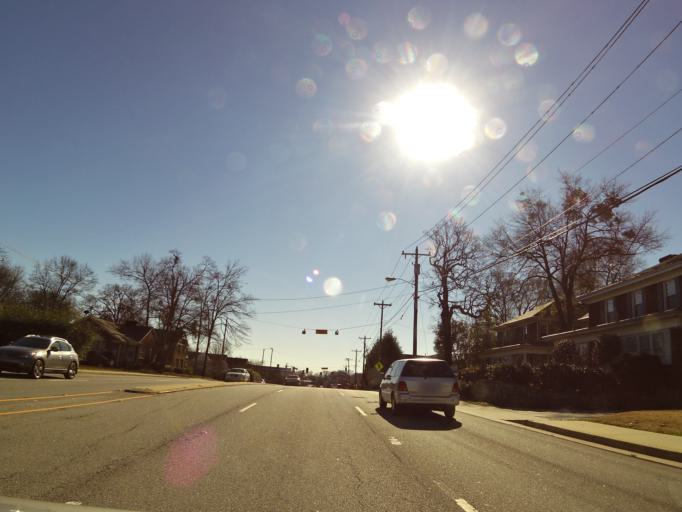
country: US
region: South Carolina
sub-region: Greenville County
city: Greenville
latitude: 34.8650
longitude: -82.4045
